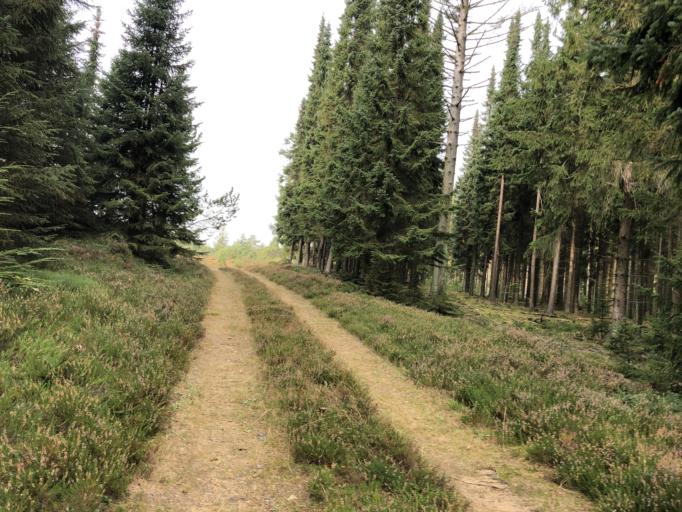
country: DK
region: Central Jutland
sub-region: Holstebro Kommune
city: Ulfborg
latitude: 56.2490
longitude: 8.4591
